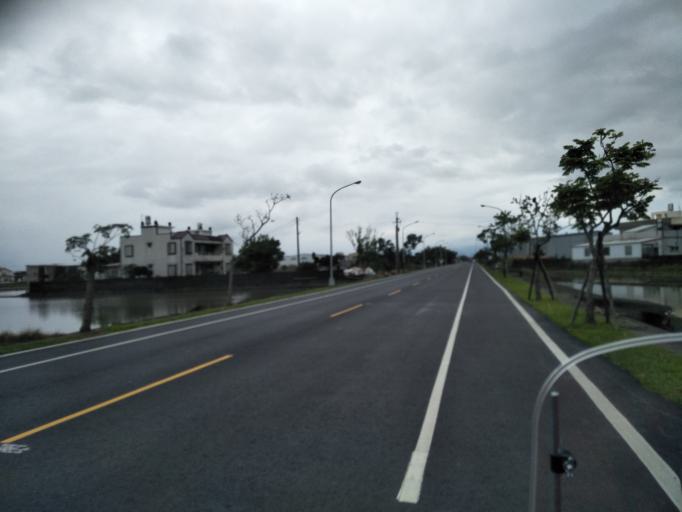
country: TW
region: Taiwan
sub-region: Yilan
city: Yilan
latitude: 24.8063
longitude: 121.7901
